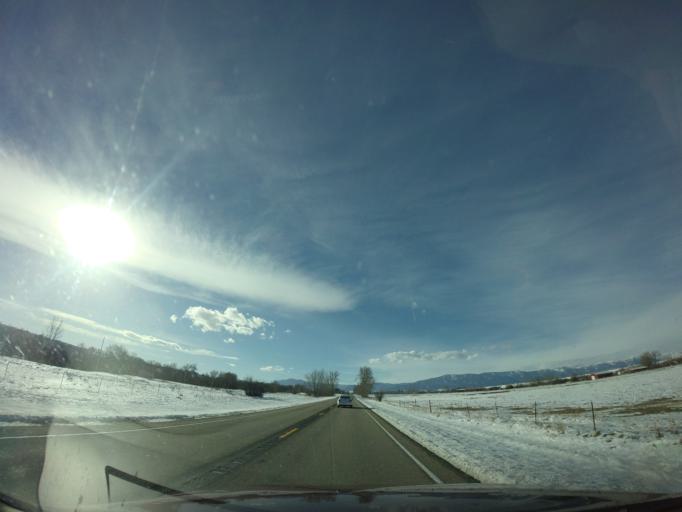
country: US
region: Montana
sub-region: Carbon County
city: Red Lodge
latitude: 45.3061
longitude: -109.2001
